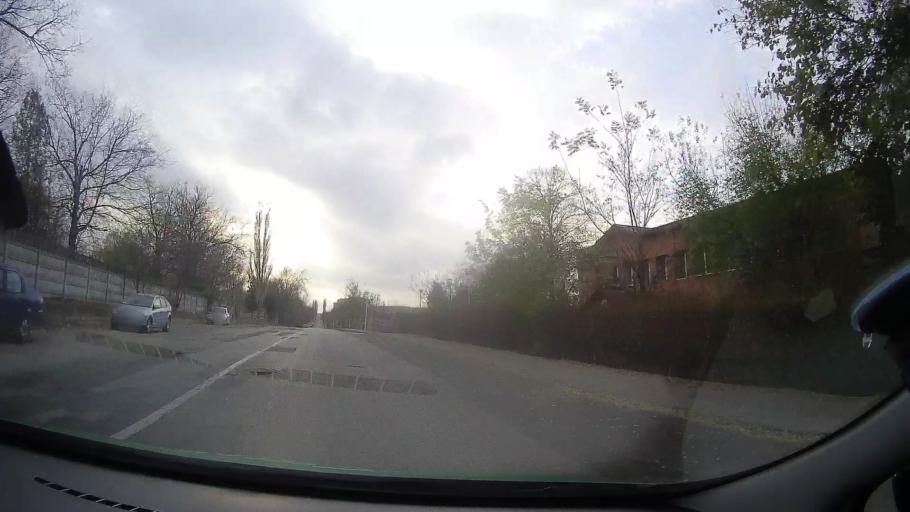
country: RO
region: Constanta
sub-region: Municipiul Medgidia
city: Medgidia
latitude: 44.2433
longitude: 28.2583
